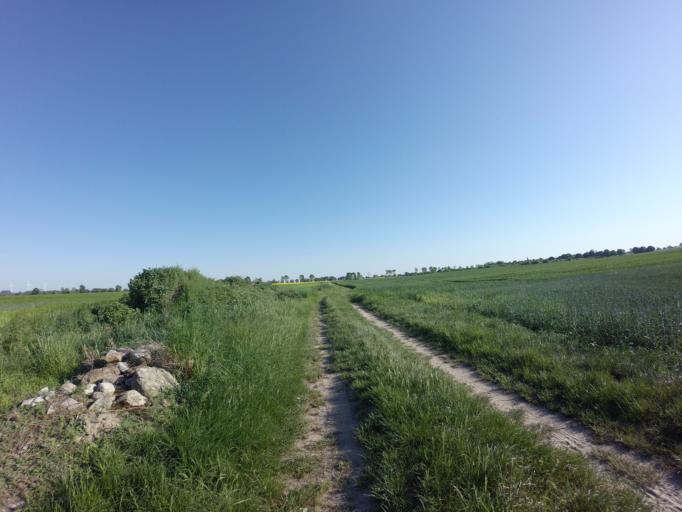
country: PL
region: West Pomeranian Voivodeship
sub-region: Powiat choszczenski
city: Choszczno
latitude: 53.1400
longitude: 15.3866
